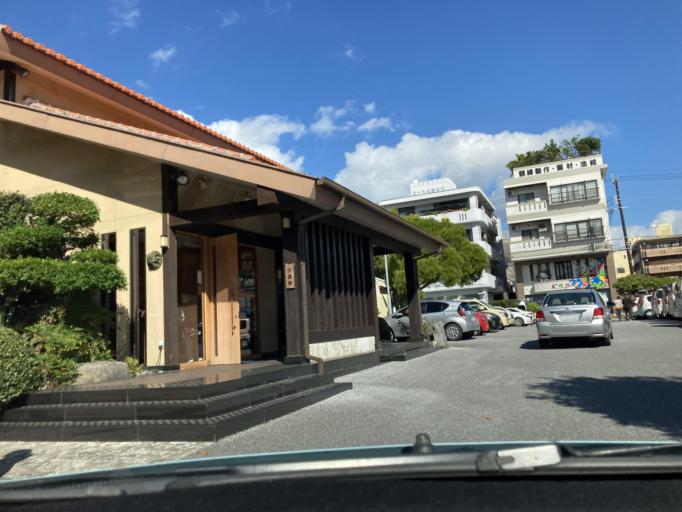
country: JP
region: Okinawa
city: Naha-shi
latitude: 26.2260
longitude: 127.6987
